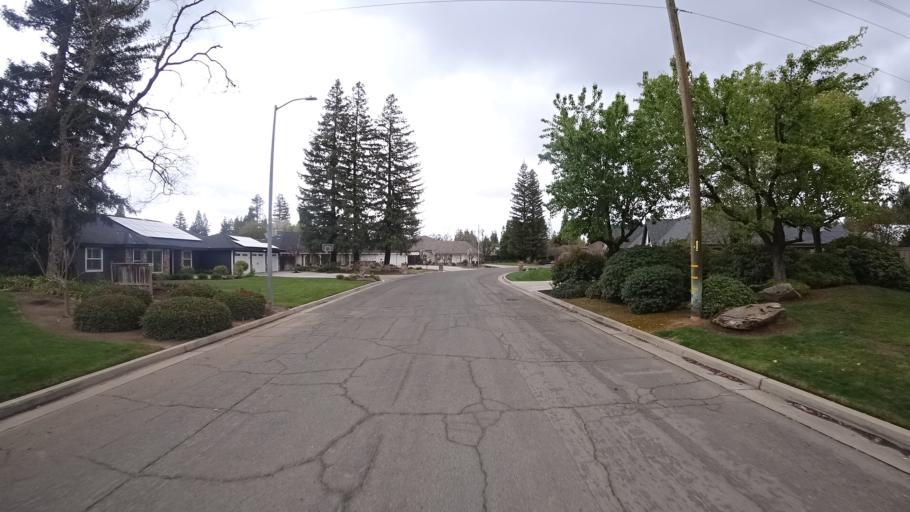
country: US
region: California
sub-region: Fresno County
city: Fresno
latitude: 36.8414
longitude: -119.8310
